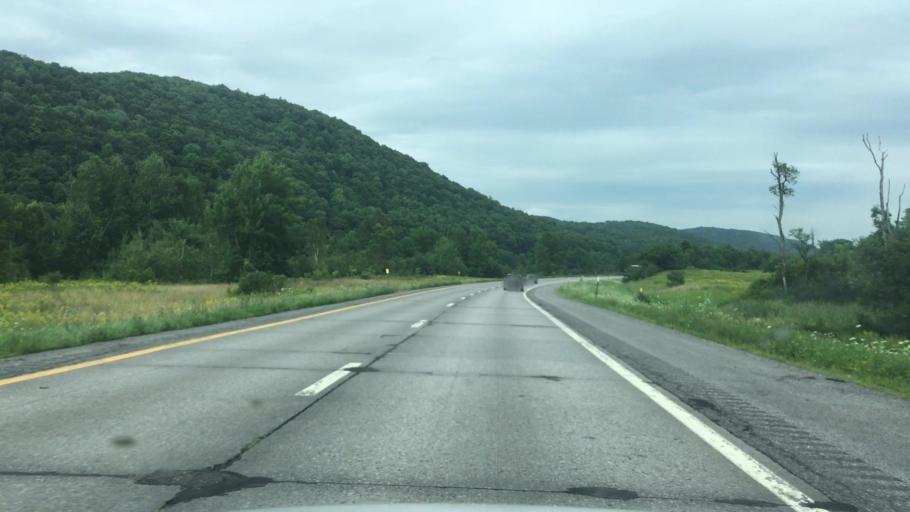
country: US
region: New York
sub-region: Otsego County
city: Worcester
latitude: 42.6014
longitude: -74.6990
